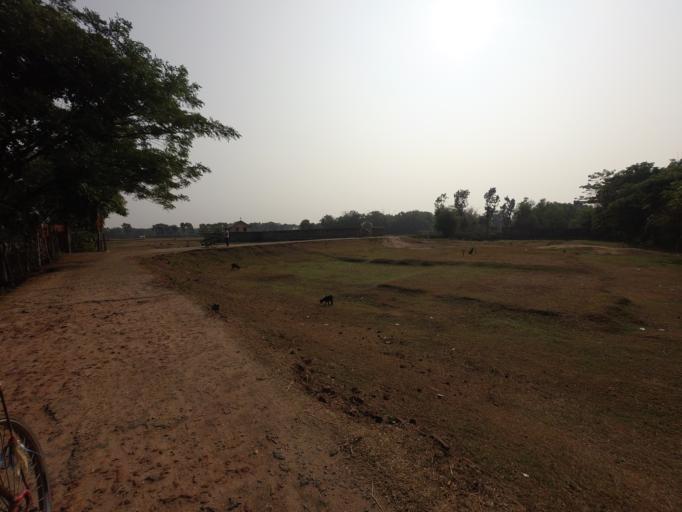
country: BD
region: Dhaka
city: Netrakona
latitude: 25.1033
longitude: 90.6754
